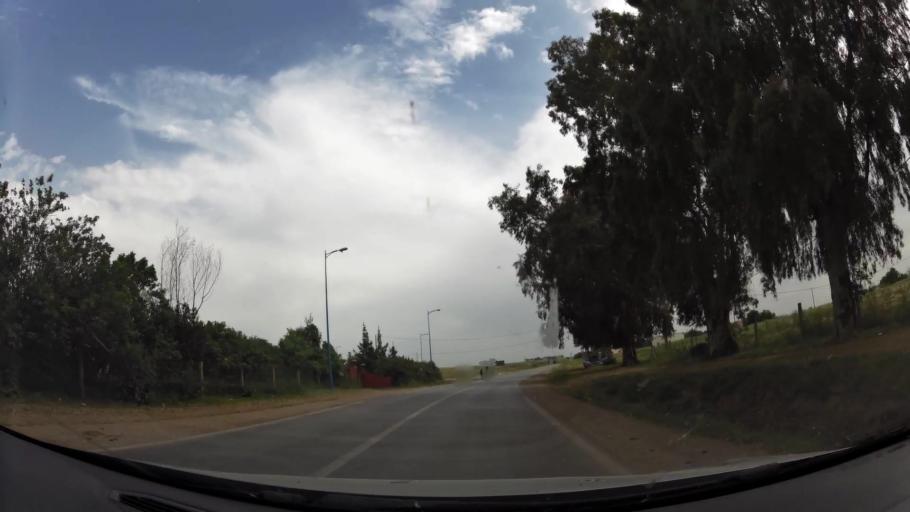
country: MA
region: Rabat-Sale-Zemmour-Zaer
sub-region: Khemisset
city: Tiflet
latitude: 33.8010
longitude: -6.2724
